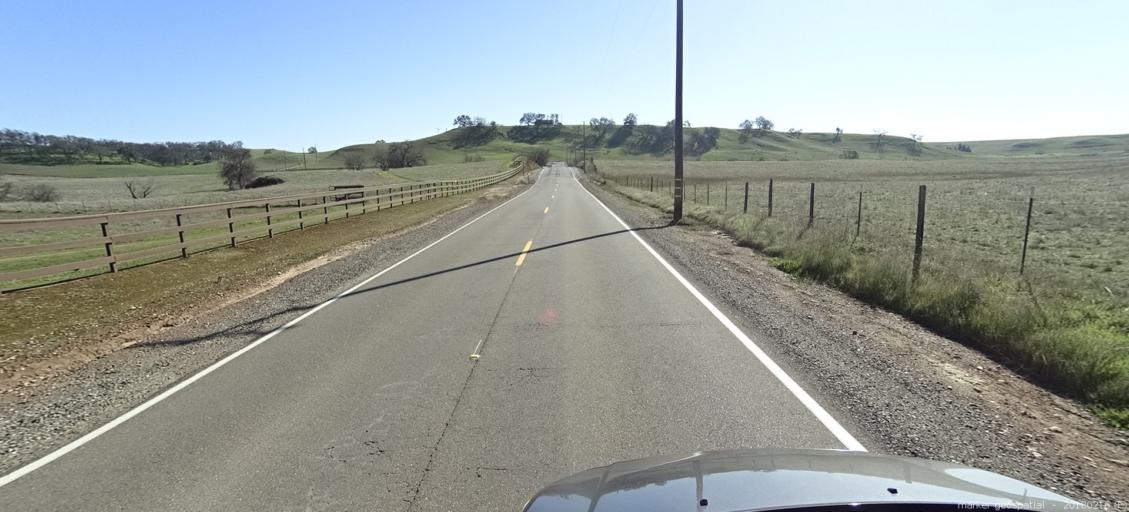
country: US
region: California
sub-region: Sacramento County
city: Rancho Murieta
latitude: 38.5224
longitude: -121.1041
